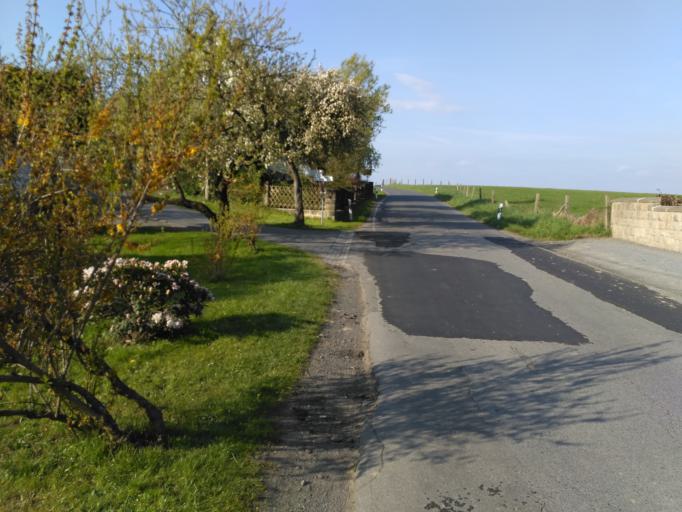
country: DE
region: Saxony
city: Durrrohrsdorf
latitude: 51.0260
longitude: 14.0040
